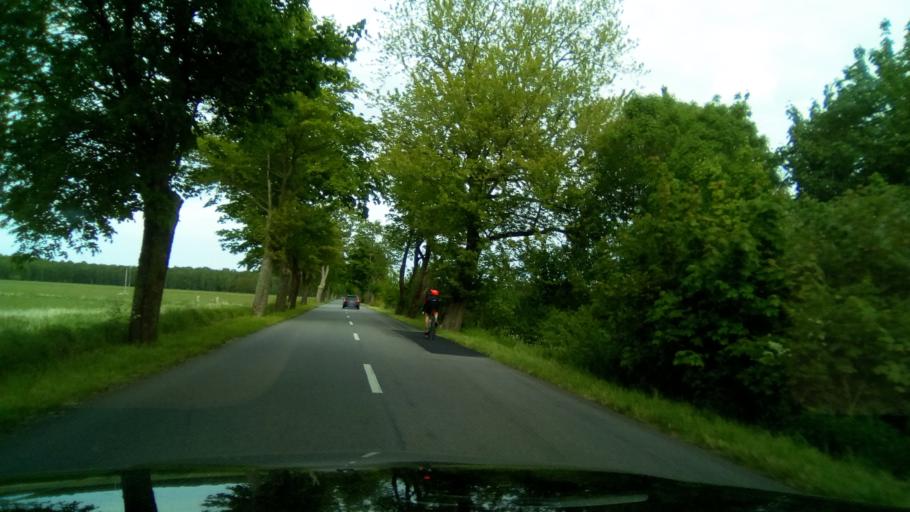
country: PL
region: Pomeranian Voivodeship
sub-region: Powiat pucki
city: Wierzchucino
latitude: 54.7930
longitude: 18.0268
